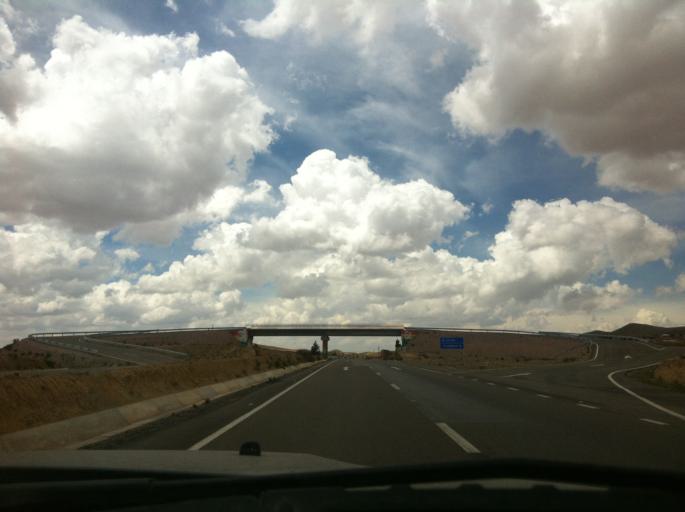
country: BO
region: La Paz
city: Patacamaya
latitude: -16.9149
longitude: -68.1165
